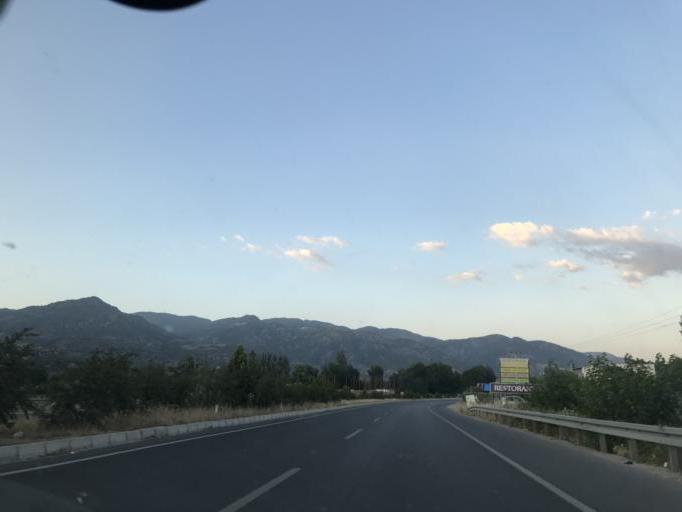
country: TR
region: Aydin
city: Buharkent
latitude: 37.9612
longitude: 28.7232
